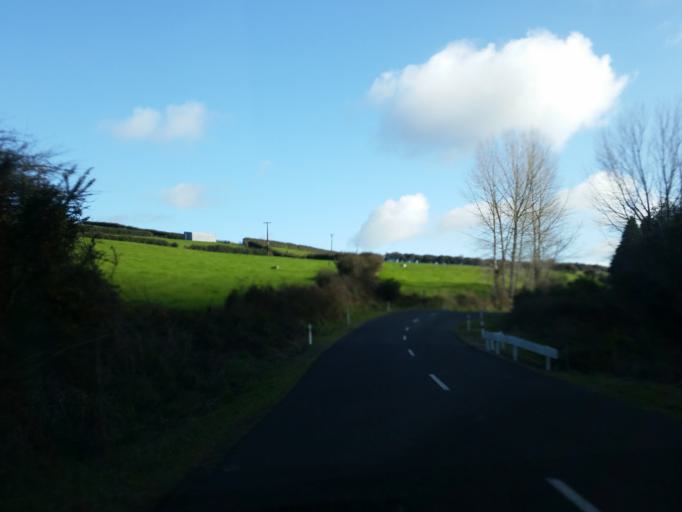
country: NZ
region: Waikato
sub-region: Hauraki District
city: Waihi
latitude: -37.4368
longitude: 175.7749
